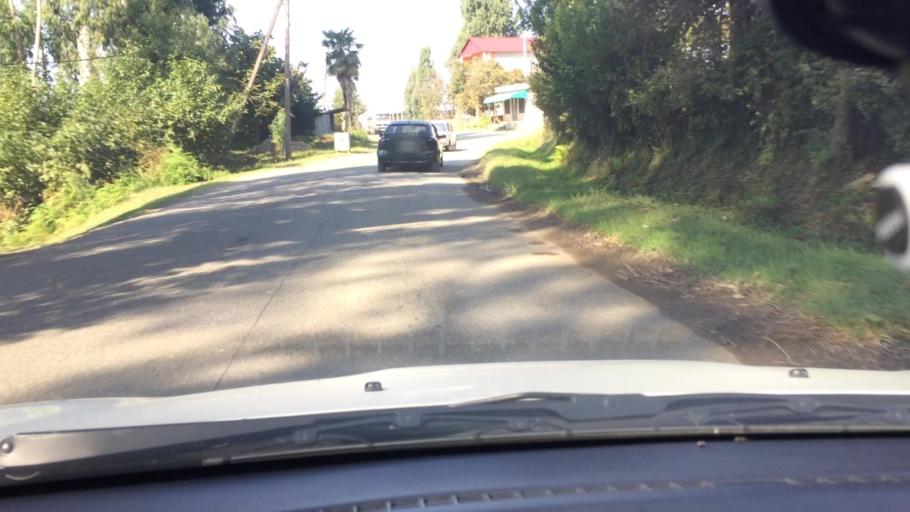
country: GE
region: Ajaria
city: Kobuleti
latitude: 41.8041
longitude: 41.8038
